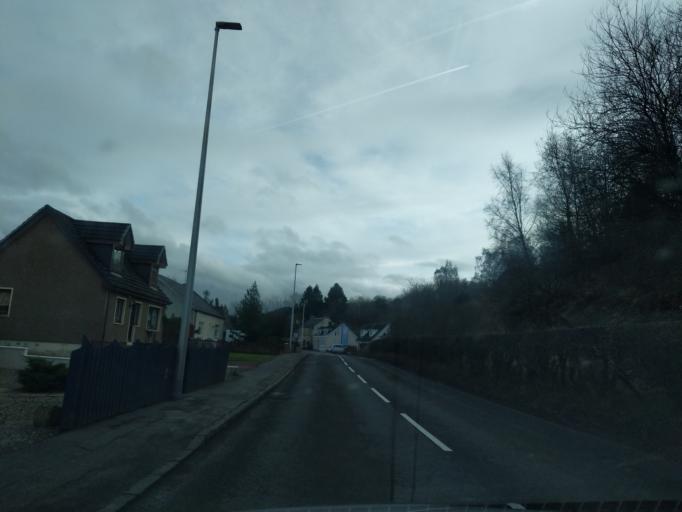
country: GB
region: Scotland
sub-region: South Lanarkshire
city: Law
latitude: 55.7012
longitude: -3.8718
